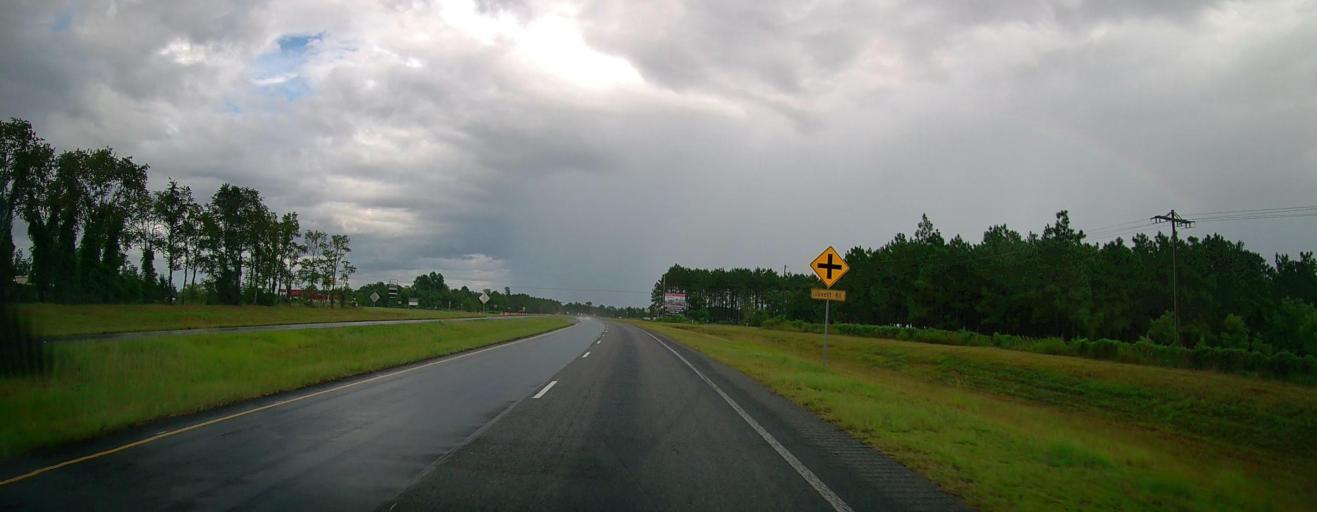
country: US
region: Georgia
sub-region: Ware County
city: Deenwood
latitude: 31.2545
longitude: -82.4733
